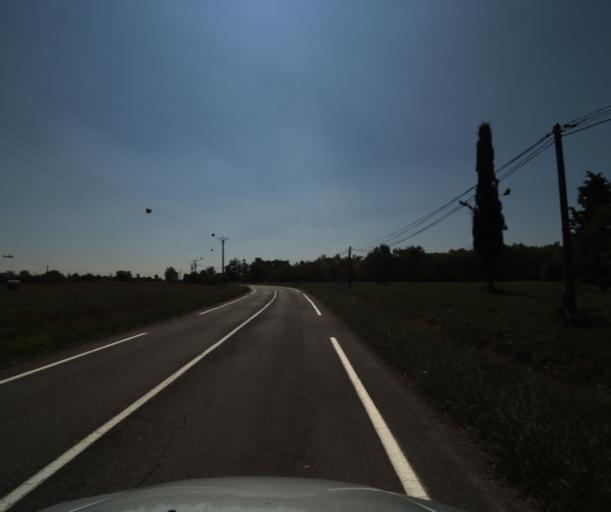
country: FR
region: Midi-Pyrenees
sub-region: Departement de la Haute-Garonne
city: Labastidette
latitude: 43.4492
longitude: 1.2748
